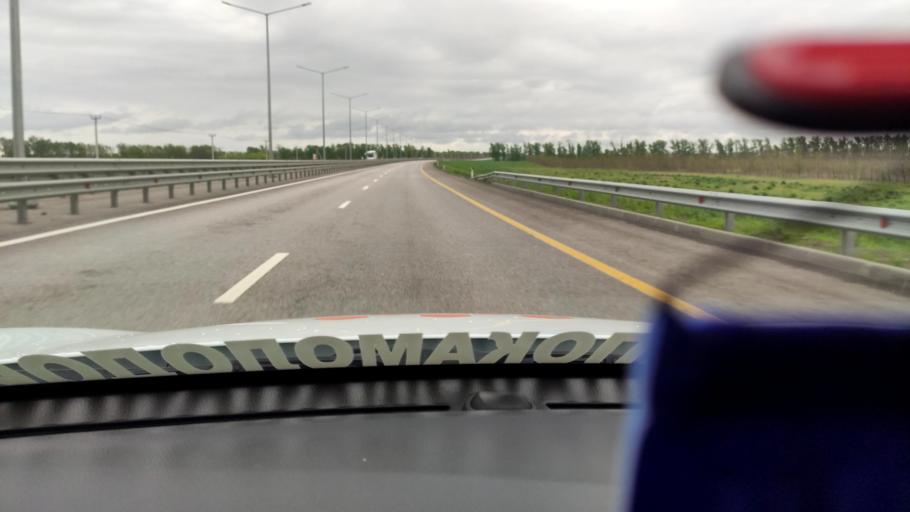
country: RU
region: Voronezj
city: Podkletnoye
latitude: 51.5834
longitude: 39.4563
